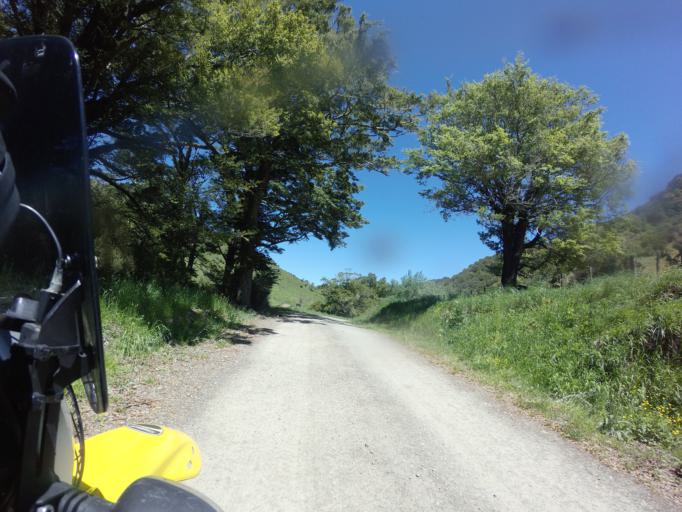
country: NZ
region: Bay of Plenty
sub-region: Opotiki District
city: Opotiki
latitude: -38.4146
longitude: 177.4072
